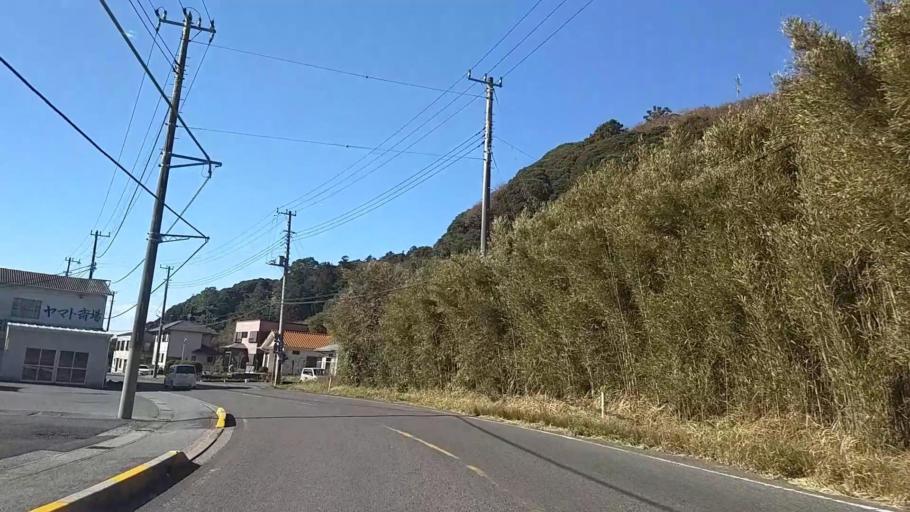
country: JP
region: Chiba
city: Tateyama
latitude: 34.9545
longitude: 139.8443
